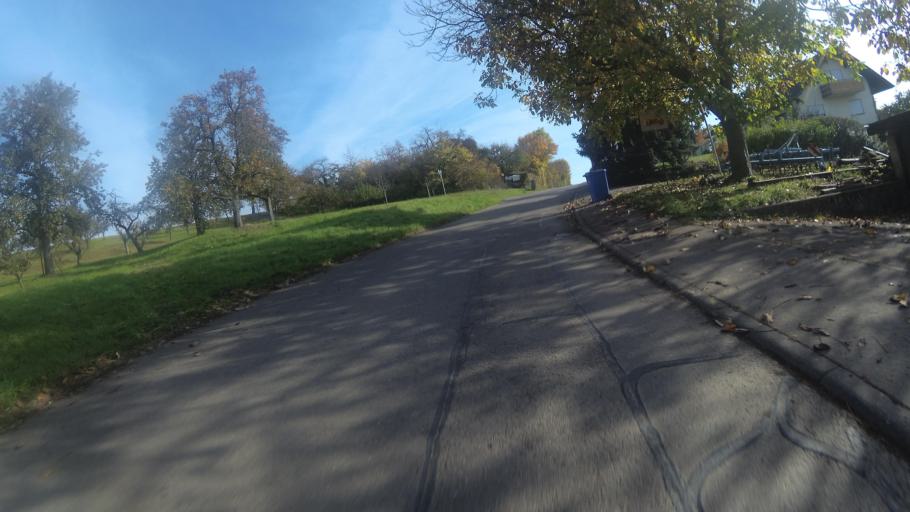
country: DE
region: Baden-Wuerttemberg
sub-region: Regierungsbezirk Stuttgart
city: Neudenau
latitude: 49.2645
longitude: 9.2852
